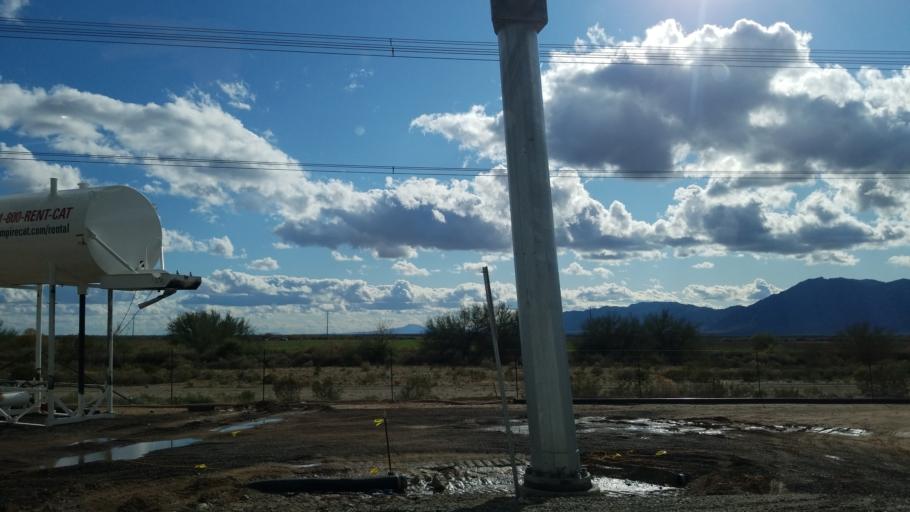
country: US
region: Arizona
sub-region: Maricopa County
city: Laveen
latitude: 33.2910
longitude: -112.1208
